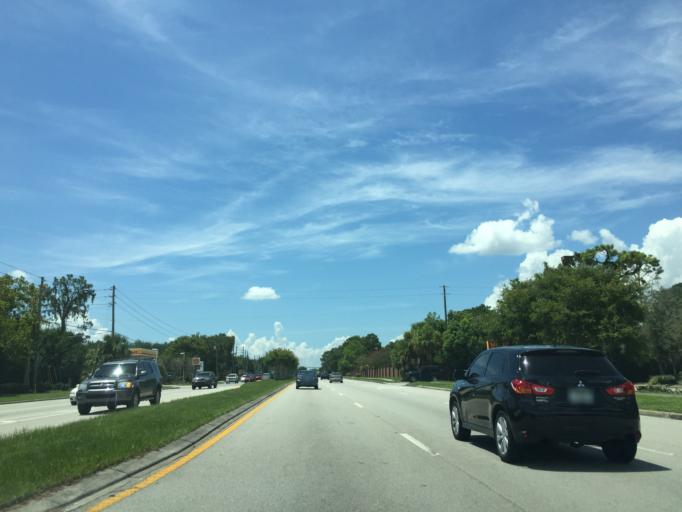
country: US
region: Florida
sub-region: Seminole County
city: Goldenrod
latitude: 28.6477
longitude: -81.2698
